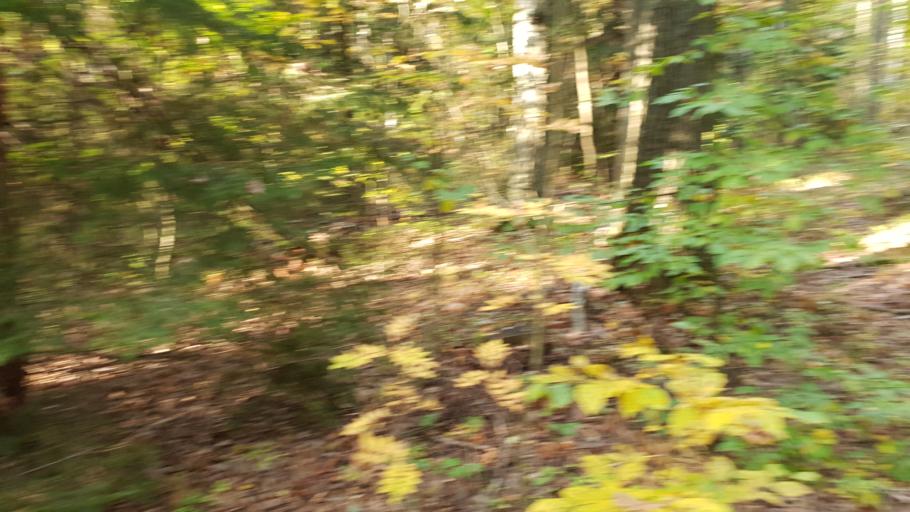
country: PL
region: Lodz Voivodeship
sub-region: Powiat zgierski
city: Zgierz
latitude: 51.8280
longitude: 19.4756
